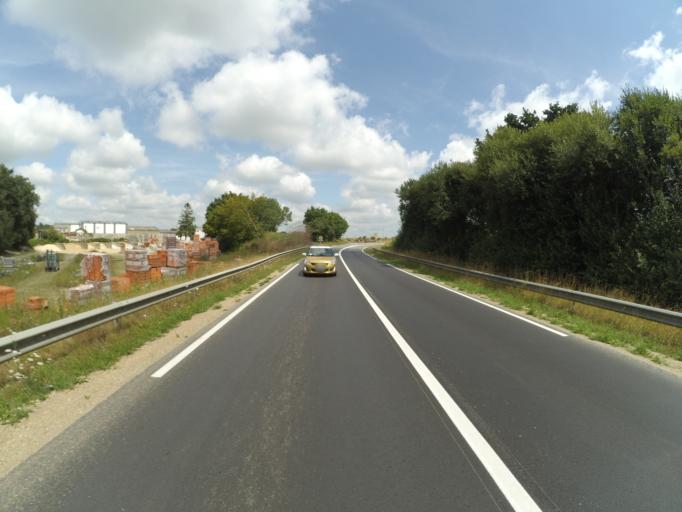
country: FR
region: Brittany
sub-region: Departement du Finistere
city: Rosporden
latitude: 47.9687
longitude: -3.8327
